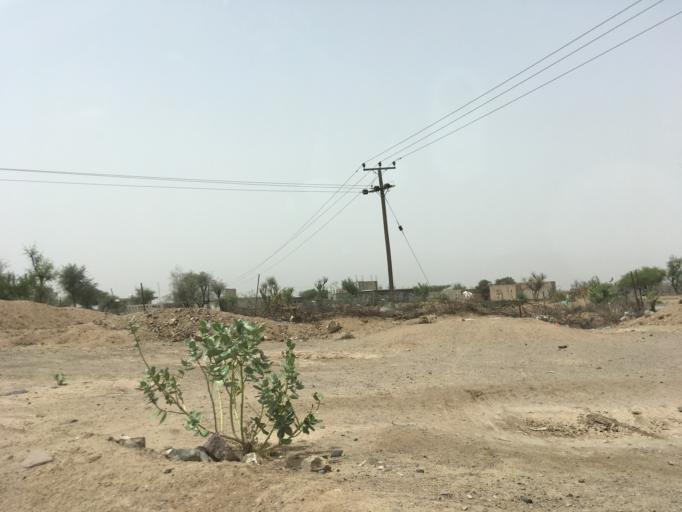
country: YE
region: Ad Dali'
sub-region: Qa'atabah
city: Qa`tabah
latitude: 13.8300
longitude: 44.7430
